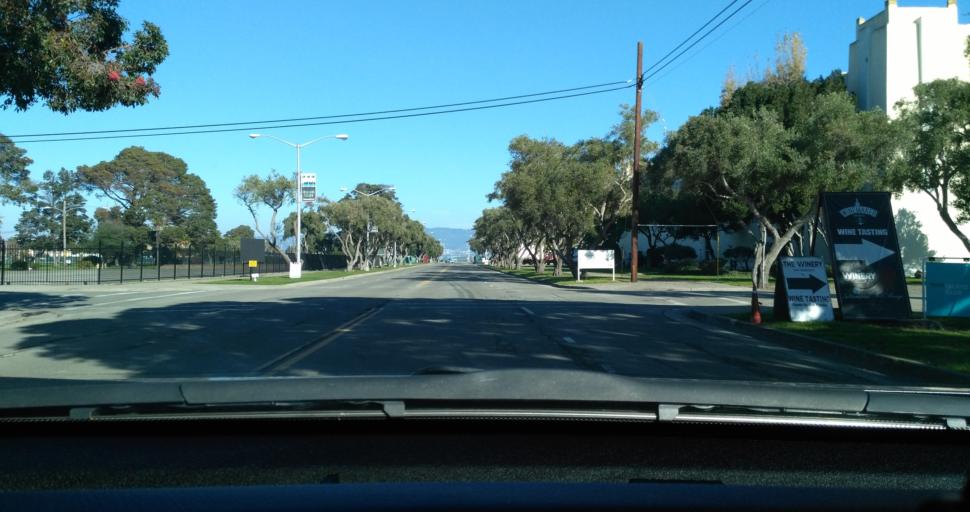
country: US
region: California
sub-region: San Francisco County
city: San Francisco
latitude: 37.8187
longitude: -122.3693
